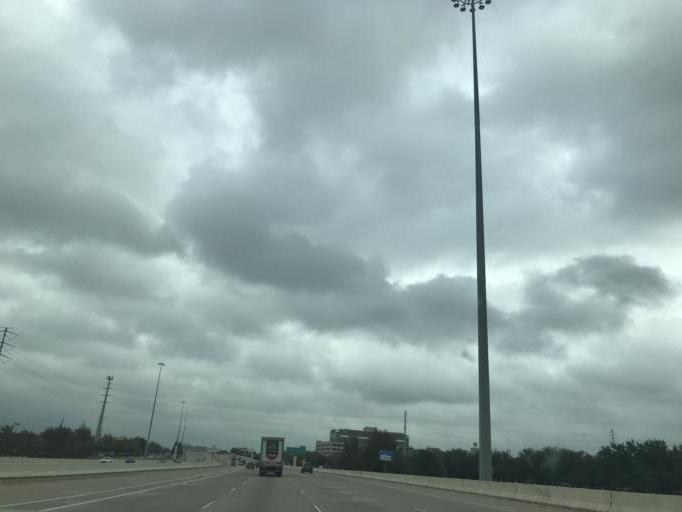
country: US
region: Texas
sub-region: Fort Bend County
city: Sugar Land
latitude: 29.5932
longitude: -95.6282
